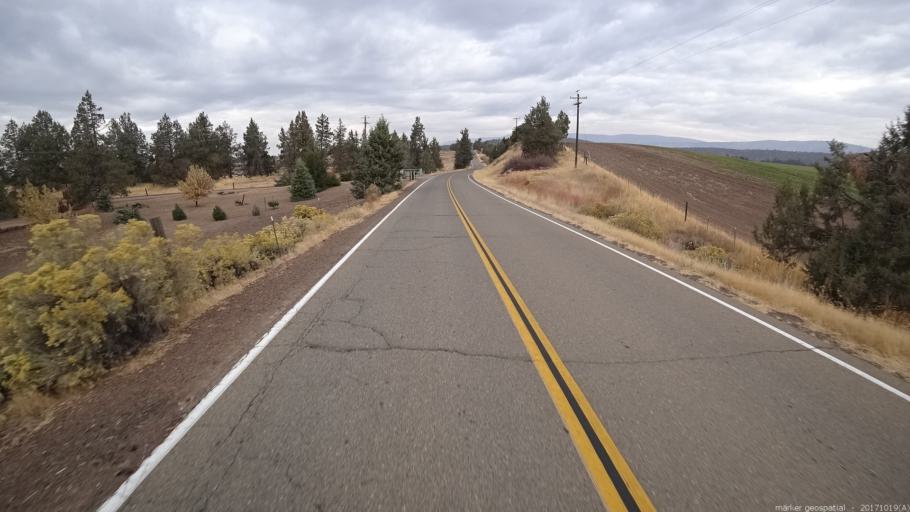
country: US
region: California
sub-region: Shasta County
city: Burney
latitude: 41.0336
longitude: -121.3315
